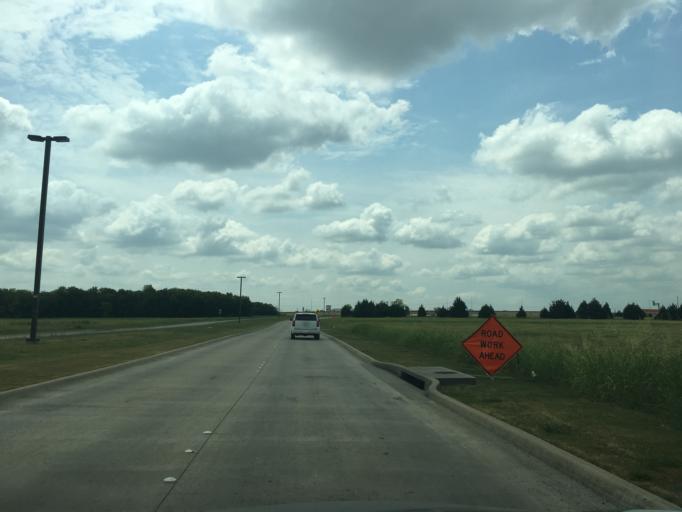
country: US
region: Texas
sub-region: Rockwall County
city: Rockwall
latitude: 32.9207
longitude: -96.4344
